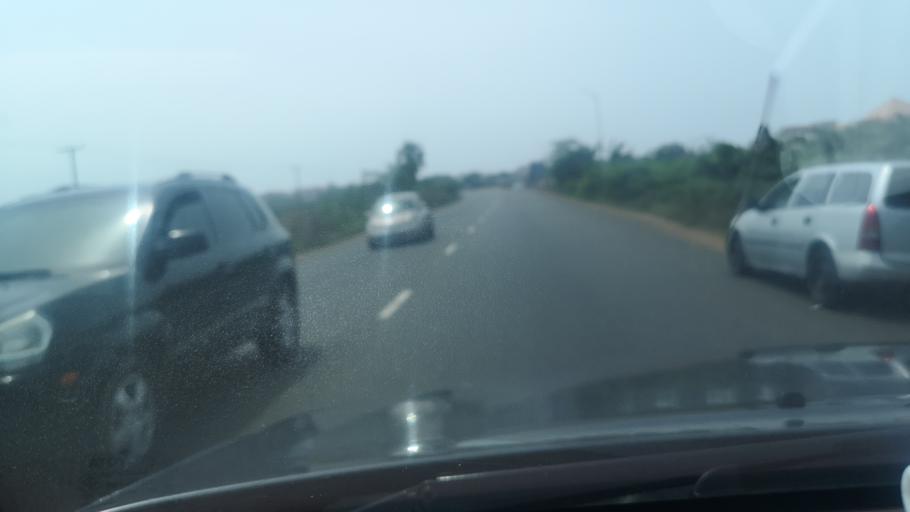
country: GH
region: Greater Accra
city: Nungua
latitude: 5.6120
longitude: -0.0546
